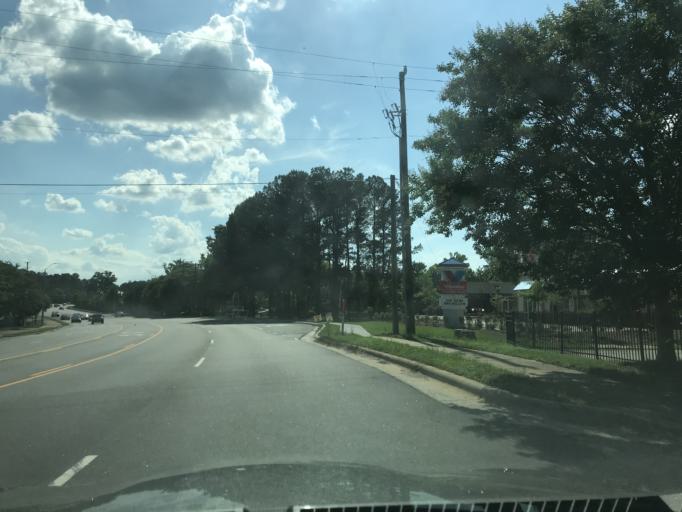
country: US
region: North Carolina
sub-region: Wake County
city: West Raleigh
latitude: 35.8957
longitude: -78.6179
